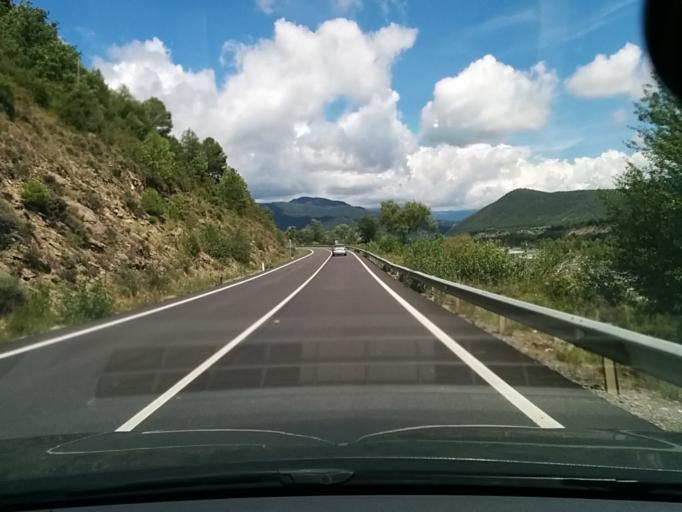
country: ES
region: Aragon
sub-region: Provincia de Huesca
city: Ainsa
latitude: 42.4202
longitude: 0.1397
